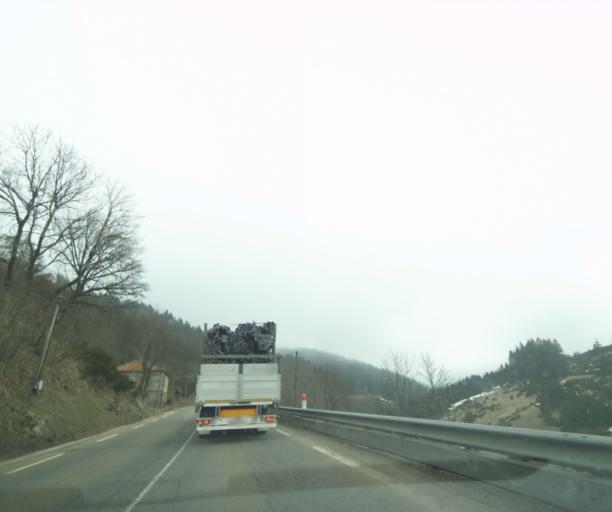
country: FR
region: Languedoc-Roussillon
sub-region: Departement de la Lozere
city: Langogne
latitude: 44.7220
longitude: 4.0053
